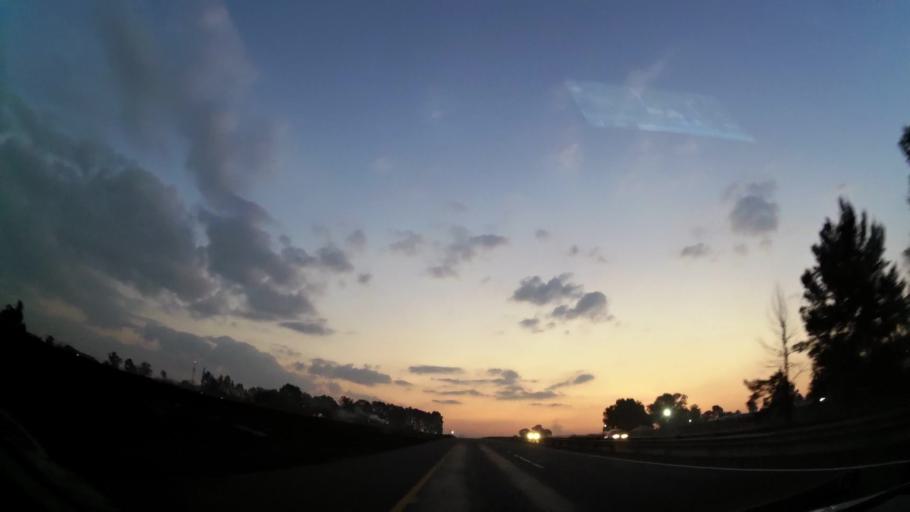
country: ZA
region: Gauteng
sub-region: Ekurhuleni Metropolitan Municipality
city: Springs
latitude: -26.2767
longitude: 28.3896
